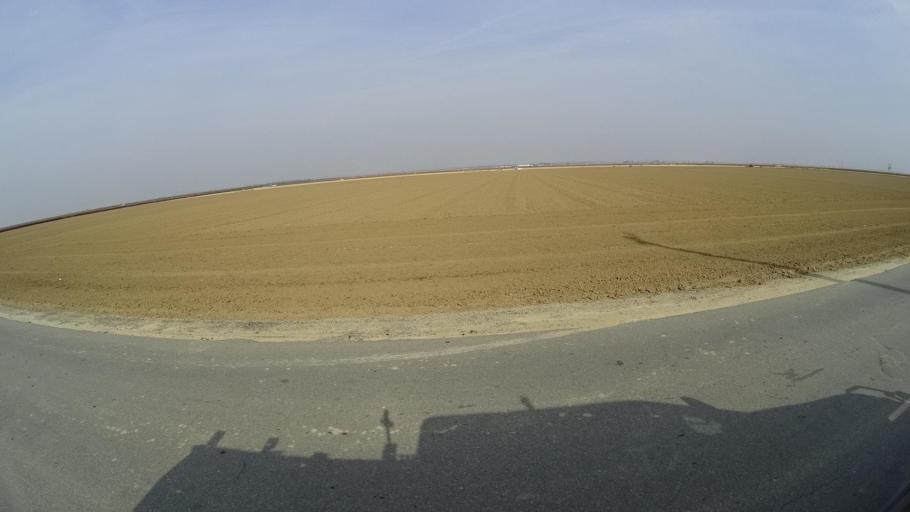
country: US
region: California
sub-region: Kern County
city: Weedpatch
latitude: 35.0749
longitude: -118.9410
